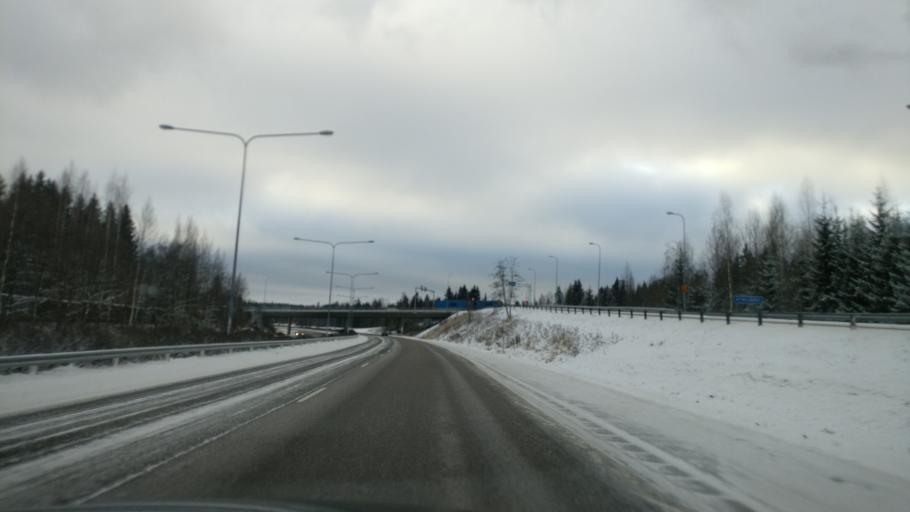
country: FI
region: Paijanne Tavastia
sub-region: Lahti
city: Lahti
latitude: 60.9876
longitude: 25.7388
